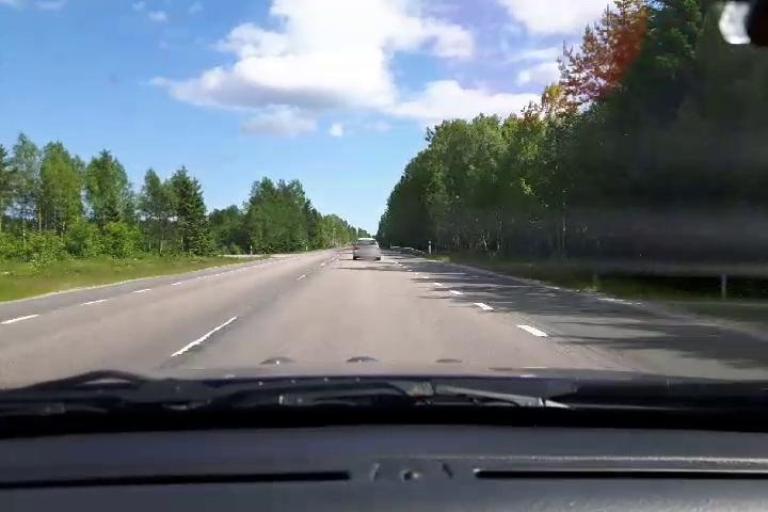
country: SE
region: Gaevleborg
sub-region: Hudiksvalls Kommun
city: Sorforsa
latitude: 61.7210
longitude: 17.0176
